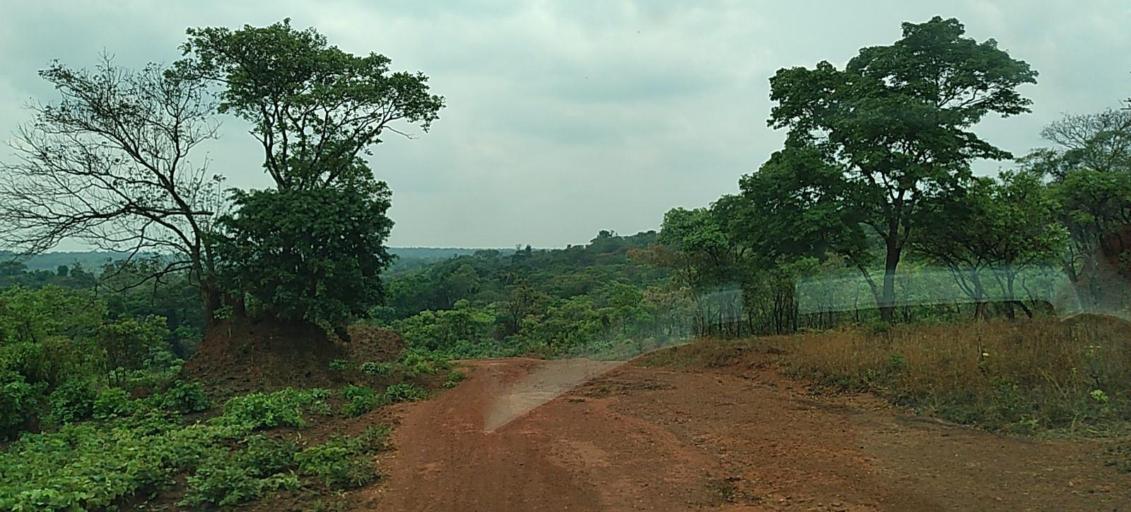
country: ZM
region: North-Western
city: Mwinilunga
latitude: -11.5129
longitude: 24.7895
